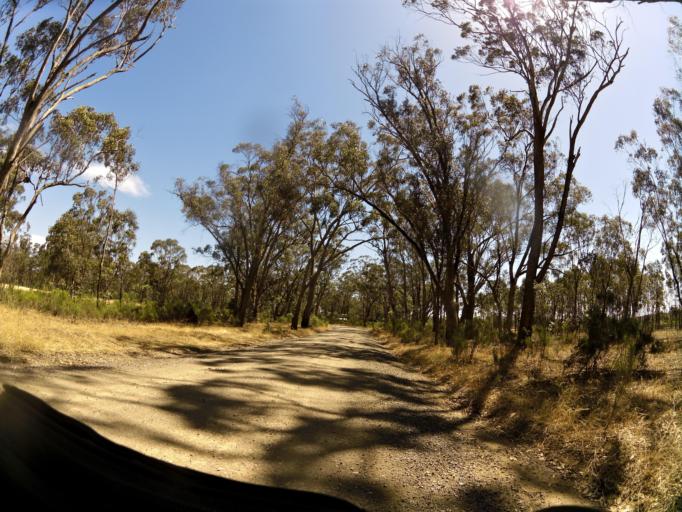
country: AU
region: Victoria
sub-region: Campaspe
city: Kyabram
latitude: -36.8419
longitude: 145.0682
